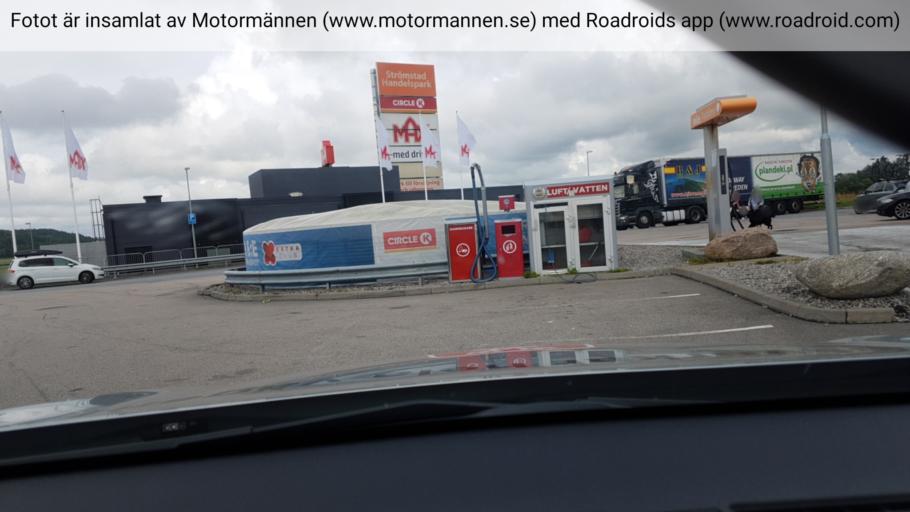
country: SE
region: Vaestra Goetaland
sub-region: Stromstads Kommun
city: Stroemstad
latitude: 58.9147
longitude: 11.2605
